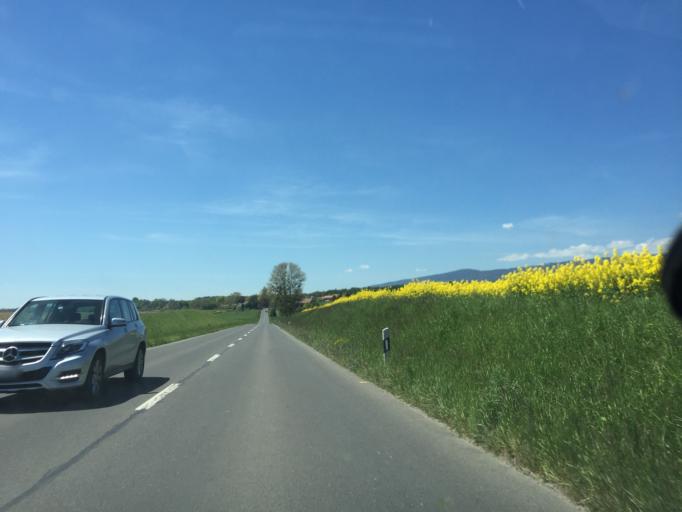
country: CH
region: Vaud
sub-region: Morges District
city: Grancy
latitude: 46.5956
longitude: 6.4770
